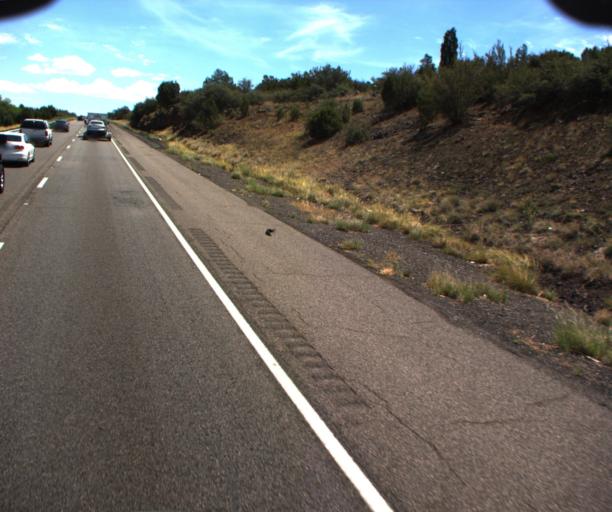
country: US
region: Arizona
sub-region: Yavapai County
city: Village of Oak Creek (Big Park)
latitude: 34.7739
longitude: -111.6345
